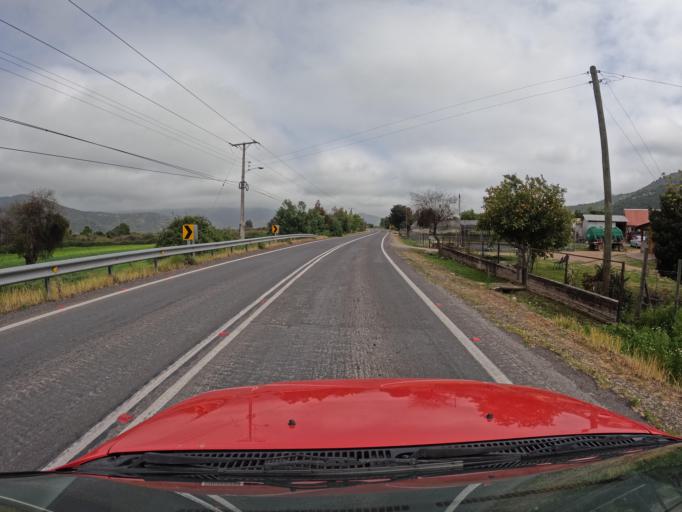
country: CL
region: Maule
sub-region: Provincia de Curico
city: Teno
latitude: -34.8085
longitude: -71.2159
